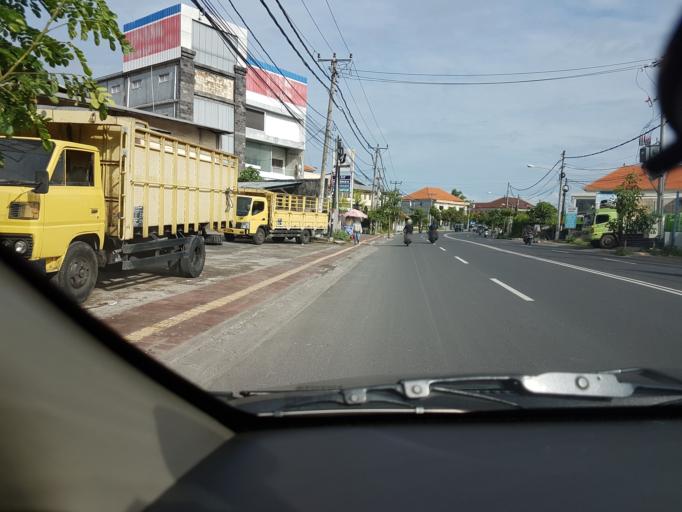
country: ID
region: Bali
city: Denpasar
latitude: -8.6756
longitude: 115.1901
